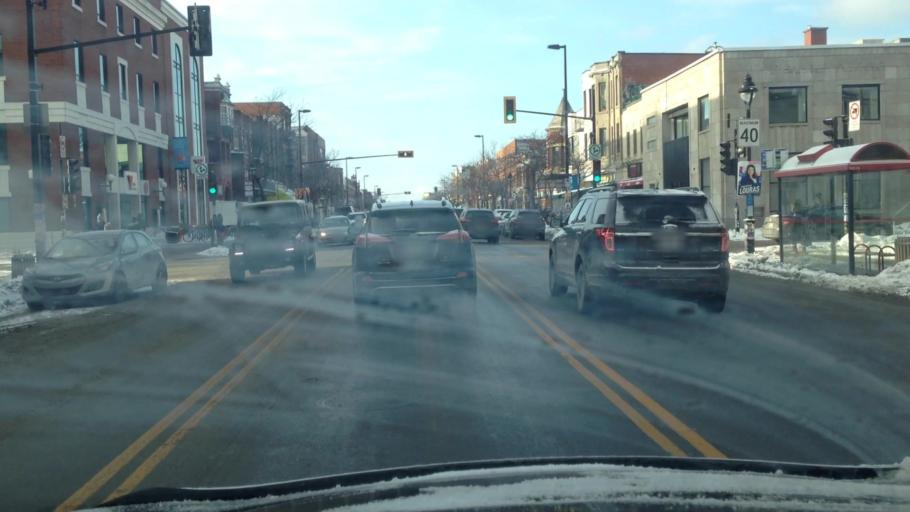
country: CA
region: Quebec
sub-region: Montreal
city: Montreal
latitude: 45.5220
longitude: -73.6017
